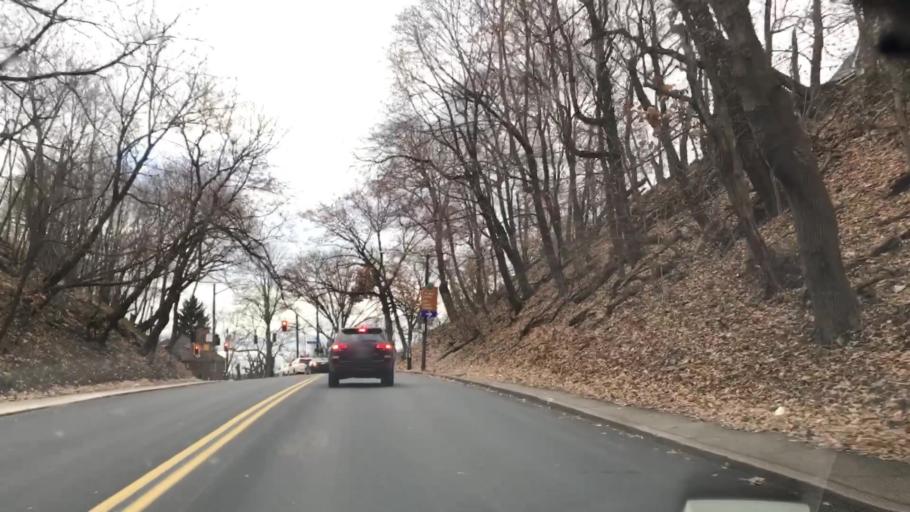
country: US
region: Pennsylvania
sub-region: Allegheny County
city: Bloomfield
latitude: 40.4485
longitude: -79.9601
